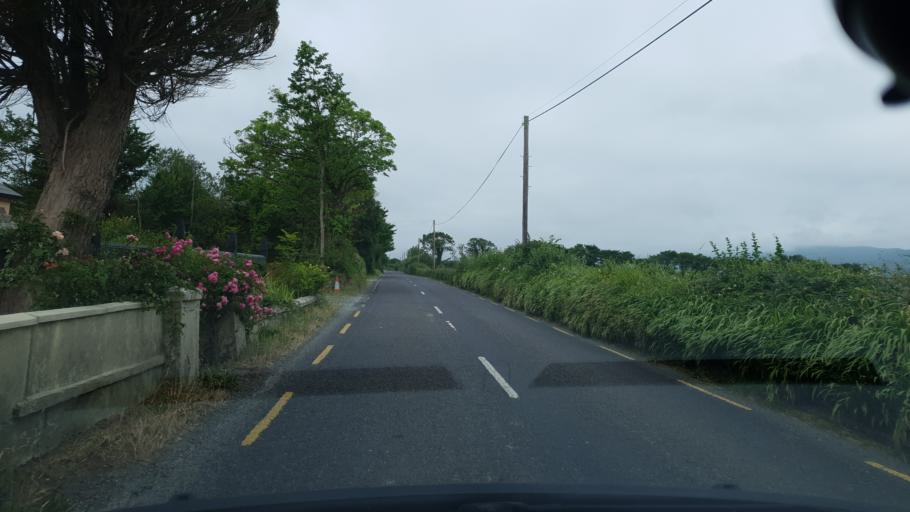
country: IE
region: Munster
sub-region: Ciarrai
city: Tralee
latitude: 52.1636
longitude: -9.6235
